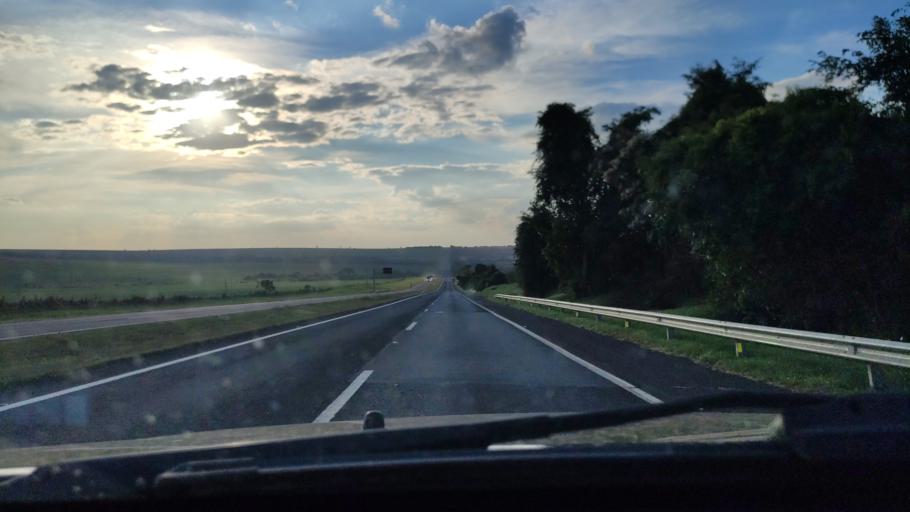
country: BR
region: Sao Paulo
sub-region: Rancharia
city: Rancharia
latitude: -22.4256
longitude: -51.0250
